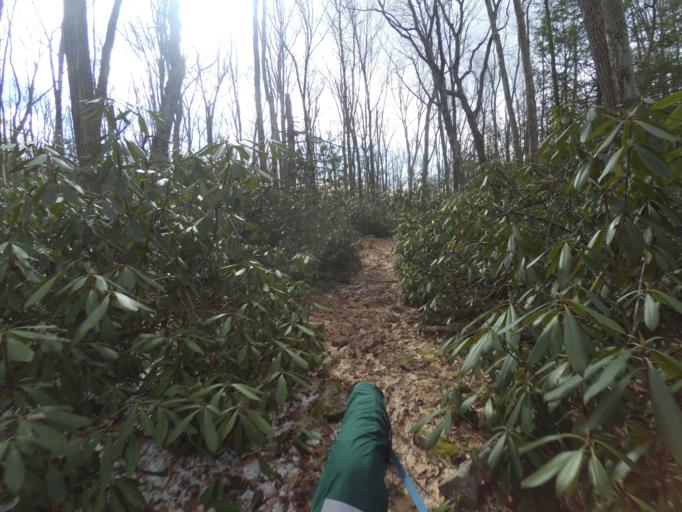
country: US
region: Pennsylvania
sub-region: Centre County
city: Boalsburg
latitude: 40.7387
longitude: -77.7345
